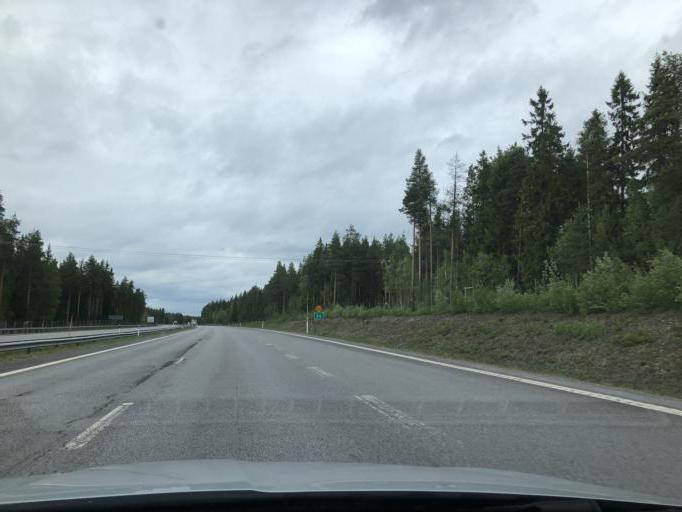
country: SE
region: Norrbotten
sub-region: Pitea Kommun
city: Pitea
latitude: 65.3361
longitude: 21.4413
